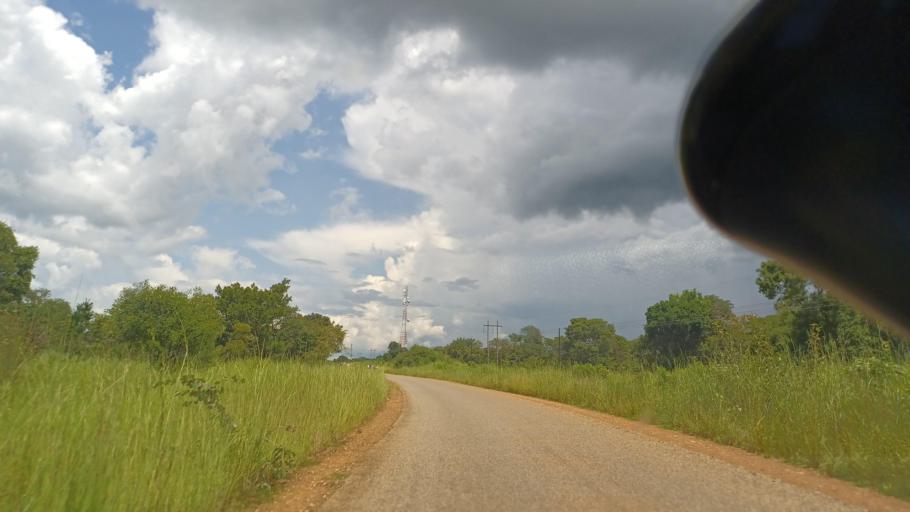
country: ZM
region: North-Western
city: Kasempa
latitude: -12.7812
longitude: 26.0090
